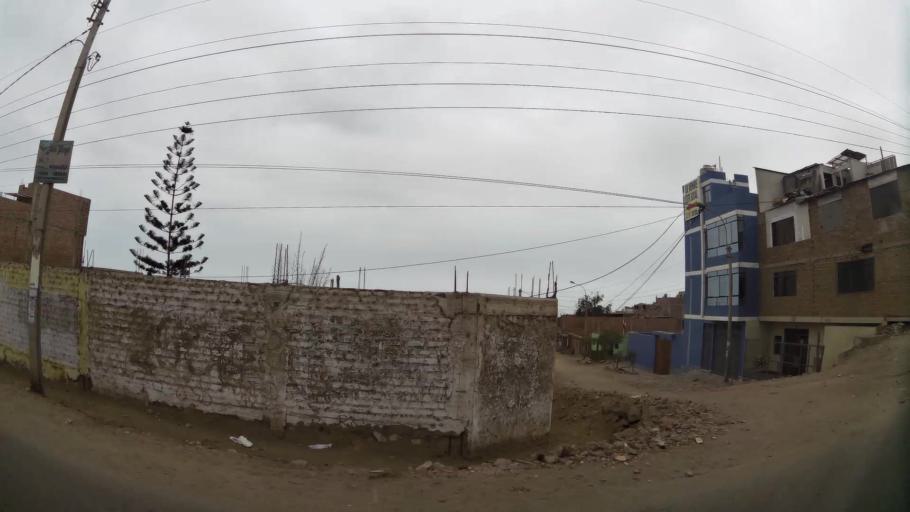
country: PE
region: Lima
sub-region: Lima
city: Surco
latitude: -12.1922
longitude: -76.9898
